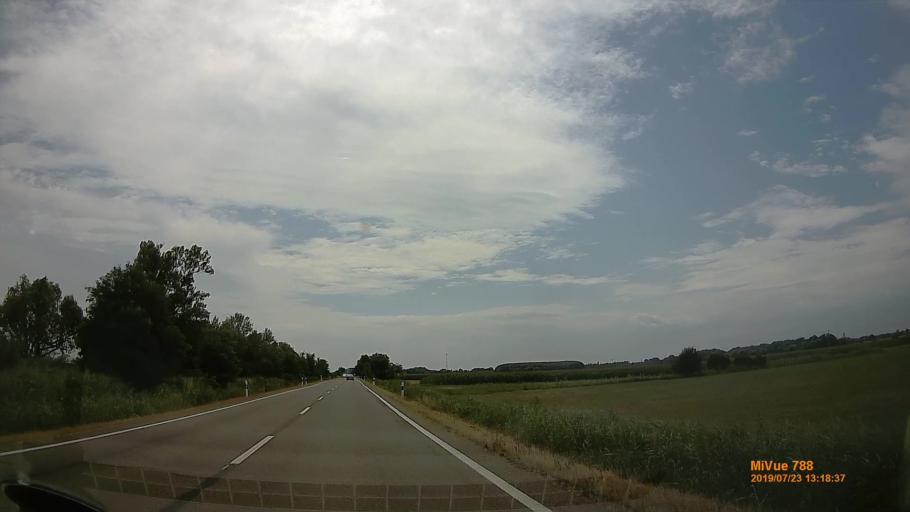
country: HU
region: Hajdu-Bihar
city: Polgar
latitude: 47.8831
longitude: 21.1479
